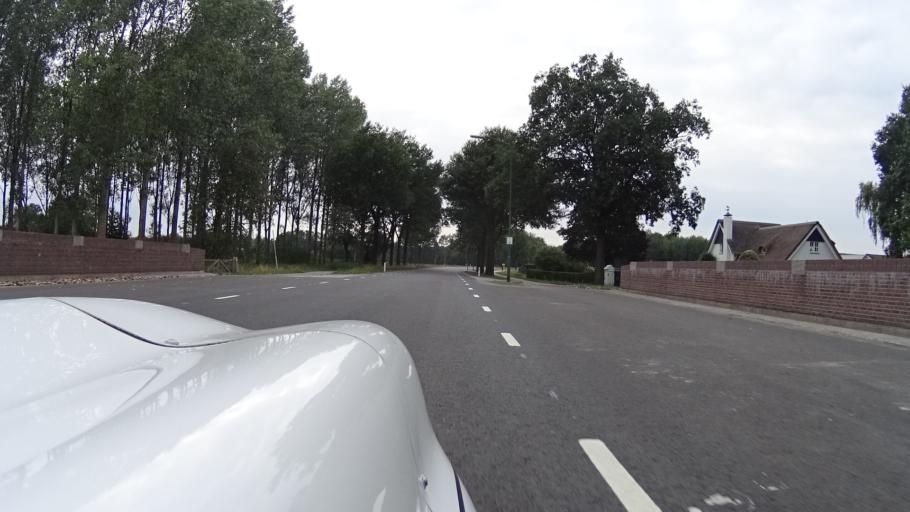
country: NL
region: North Brabant
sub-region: Gemeente Boekel
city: Boekel
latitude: 51.5737
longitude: 5.6563
